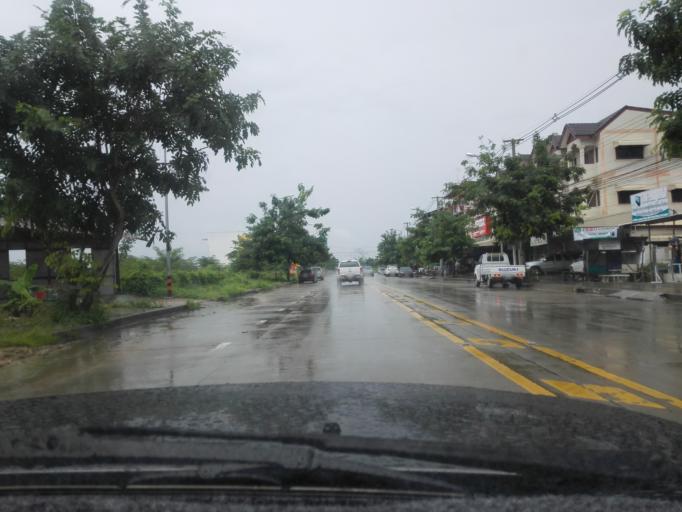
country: TH
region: Tak
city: Mae Sot
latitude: 16.7139
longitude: 98.5840
